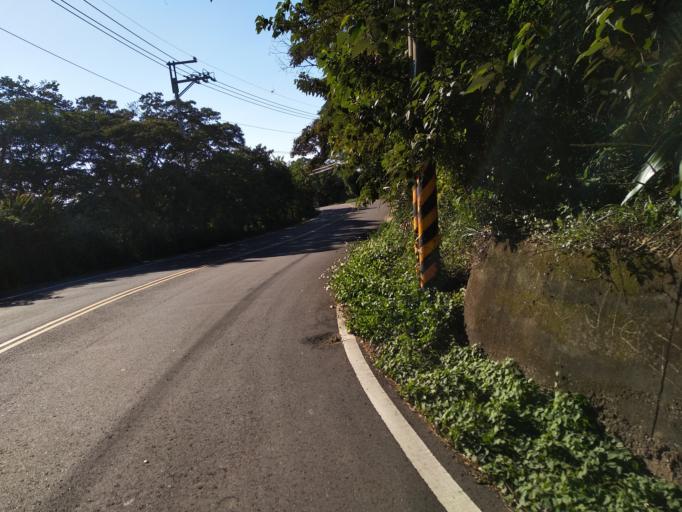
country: TW
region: Taiwan
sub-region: Hsinchu
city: Zhubei
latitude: 24.8688
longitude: 121.0947
